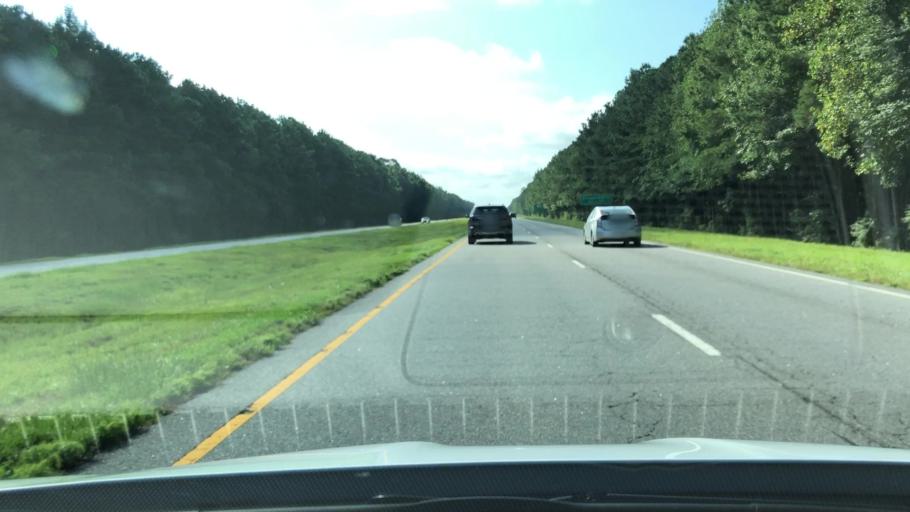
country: US
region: North Carolina
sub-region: Pasquotank County
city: Elizabeth City
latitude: 36.3967
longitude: -76.3283
